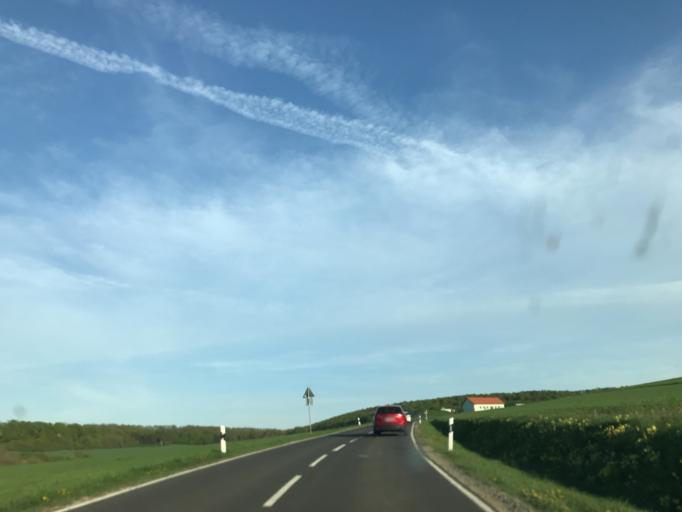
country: DE
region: Thuringia
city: Heuthen
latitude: 51.3411
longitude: 10.2282
